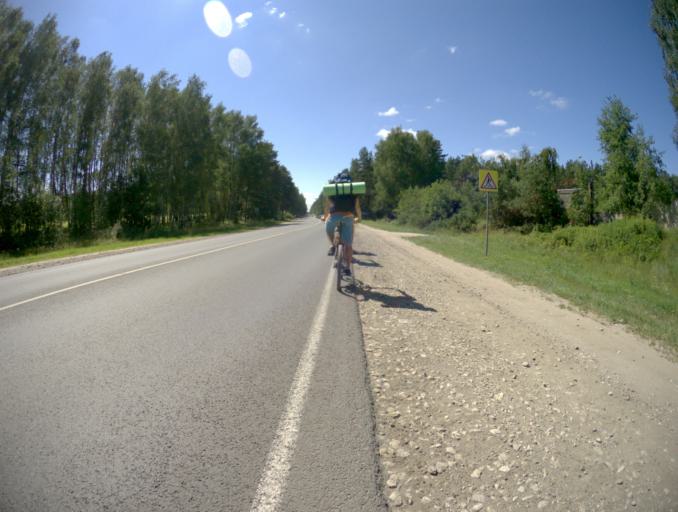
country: RU
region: Nizjnij Novgorod
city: Neklyudovo
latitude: 56.4443
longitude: 44.0058
